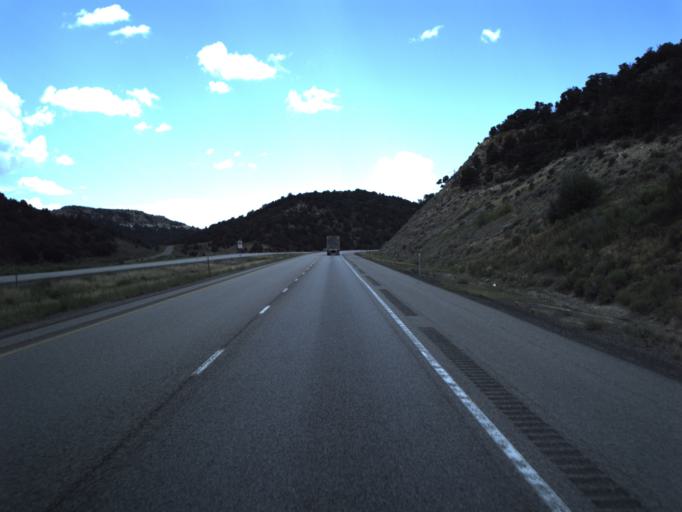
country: US
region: Utah
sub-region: Wayne County
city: Loa
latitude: 38.7651
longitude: -111.4667
